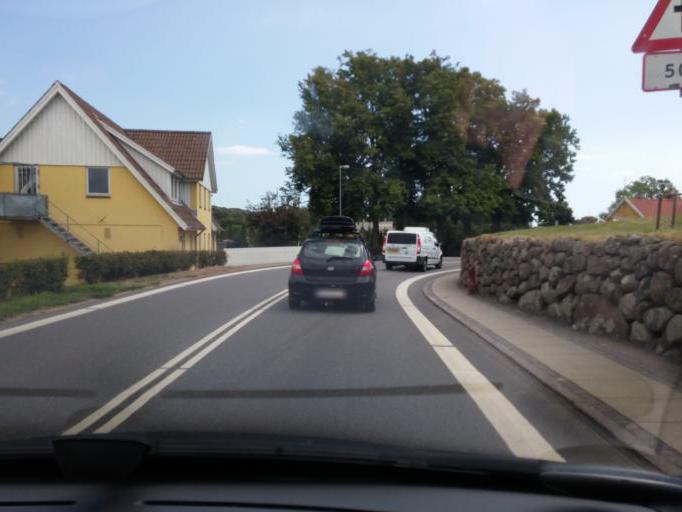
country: DK
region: South Denmark
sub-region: Langeland Kommune
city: Rudkobing
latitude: 54.8651
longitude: 10.7298
